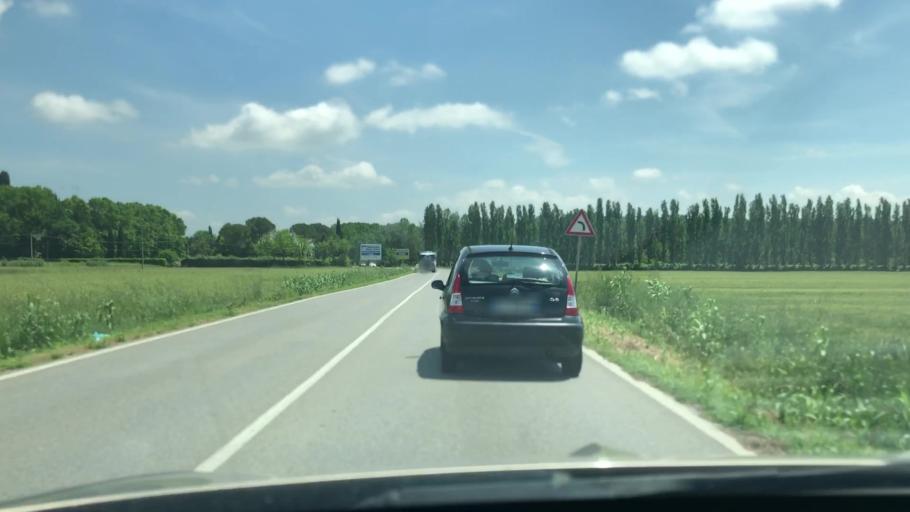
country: IT
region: Tuscany
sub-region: Province of Pisa
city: Treggiaia
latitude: 43.6168
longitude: 10.6766
